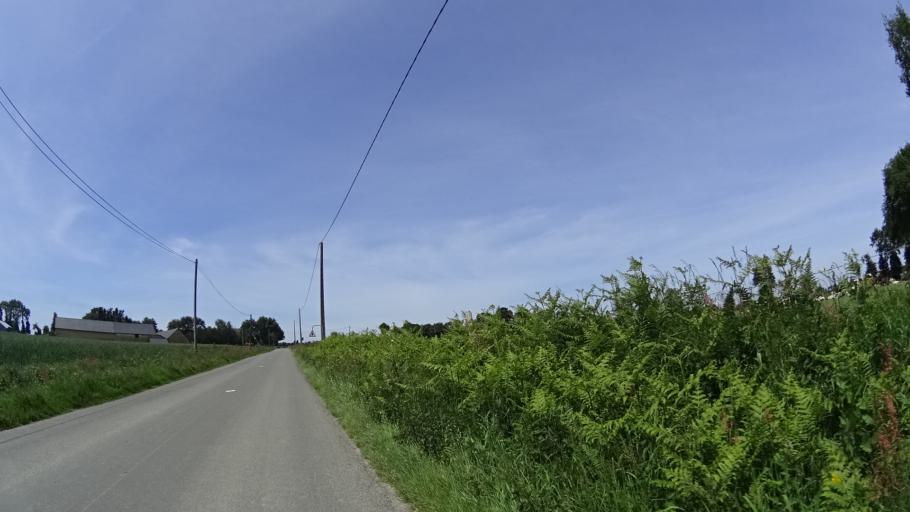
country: FR
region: Brittany
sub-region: Departement d'Ille-et-Vilaine
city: Romille
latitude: 48.1962
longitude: -1.8484
